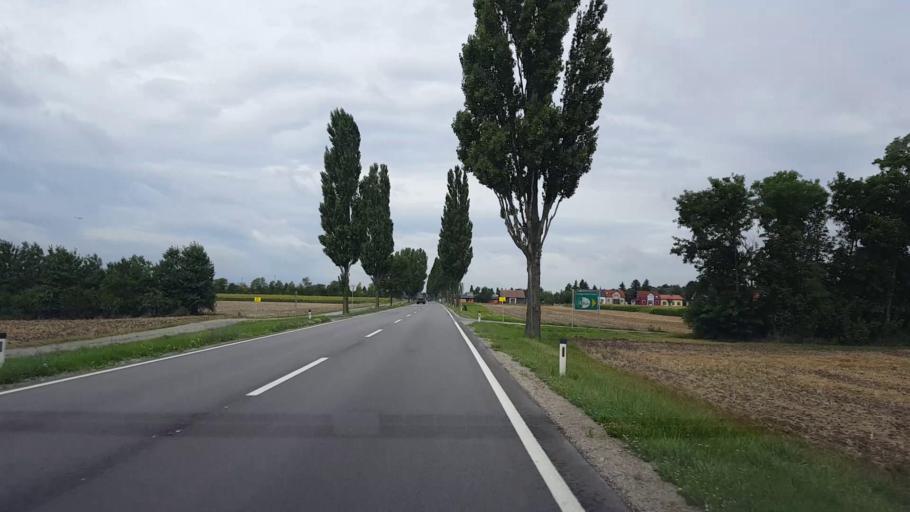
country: AT
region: Lower Austria
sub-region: Politischer Bezirk Bruck an der Leitha
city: Trautmannsdorf an der Leitha
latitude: 48.0495
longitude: 16.6489
